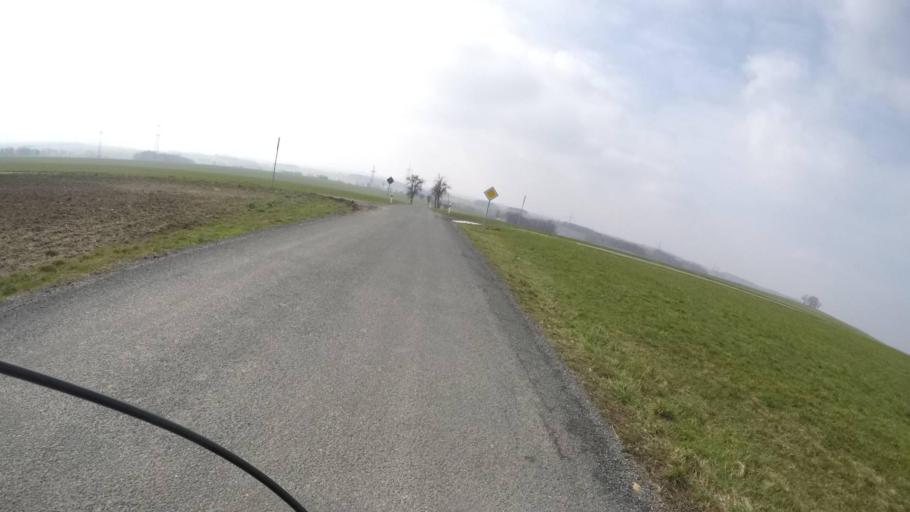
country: DE
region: Saxony
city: Niederfrohna
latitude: 50.8823
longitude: 12.6996
